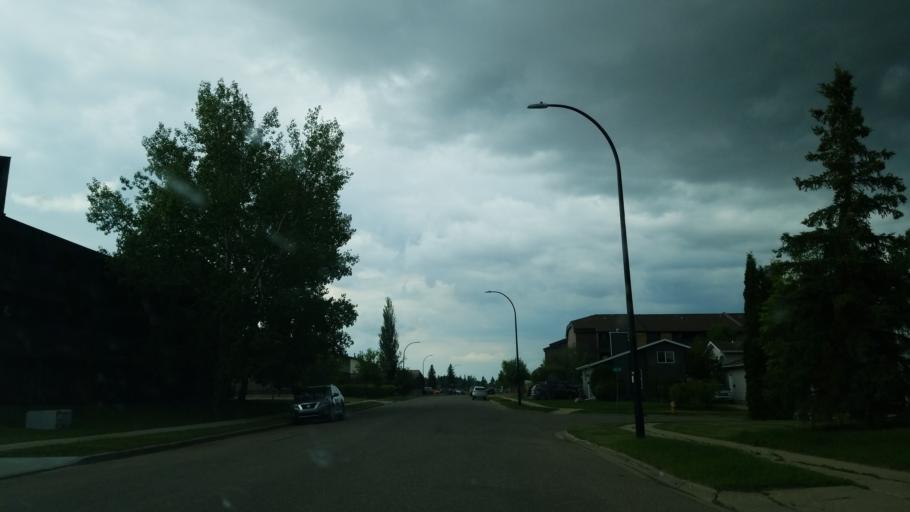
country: CA
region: Saskatchewan
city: Lloydminster
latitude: 53.2648
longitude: -110.0213
